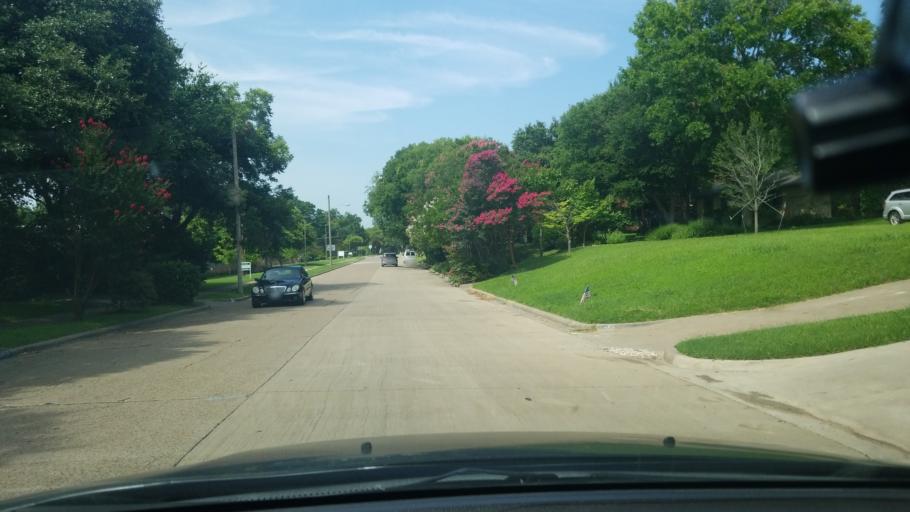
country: US
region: Texas
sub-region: Dallas County
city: Highland Park
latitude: 32.8149
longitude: -96.7093
